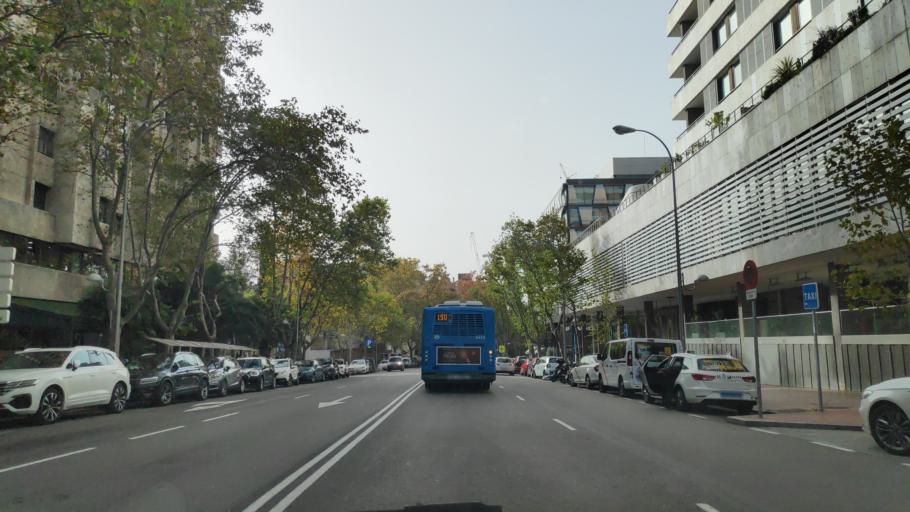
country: ES
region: Madrid
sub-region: Provincia de Madrid
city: Chamartin
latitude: 40.4585
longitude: -3.6856
